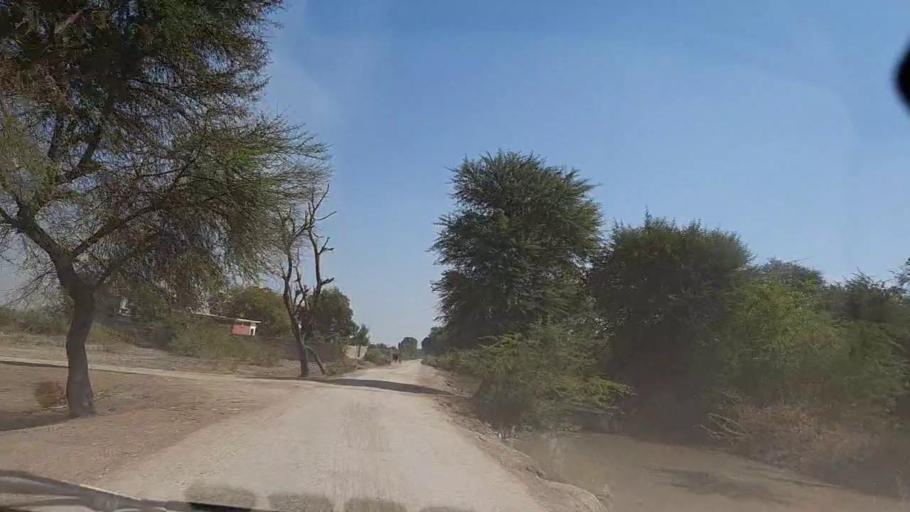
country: PK
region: Sindh
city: Mirpur Khas
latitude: 25.4293
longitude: 69.0245
